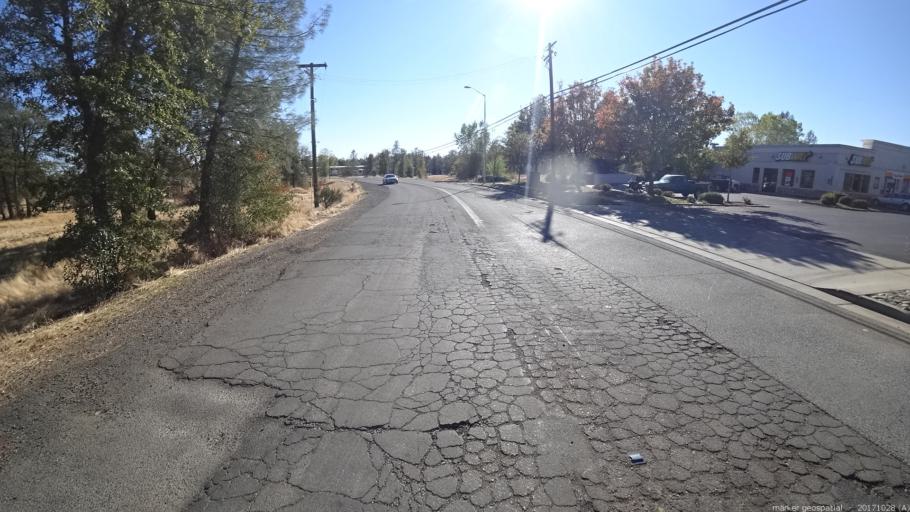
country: US
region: California
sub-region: Shasta County
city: Shasta Lake
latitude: 40.6418
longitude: -122.3671
